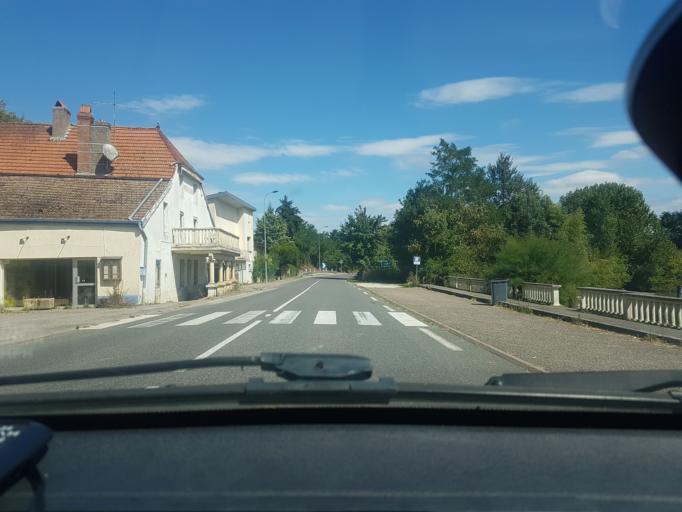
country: FR
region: Franche-Comte
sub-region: Departement de la Haute-Saone
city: Gray-la-Ville
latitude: 47.4489
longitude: 5.5614
